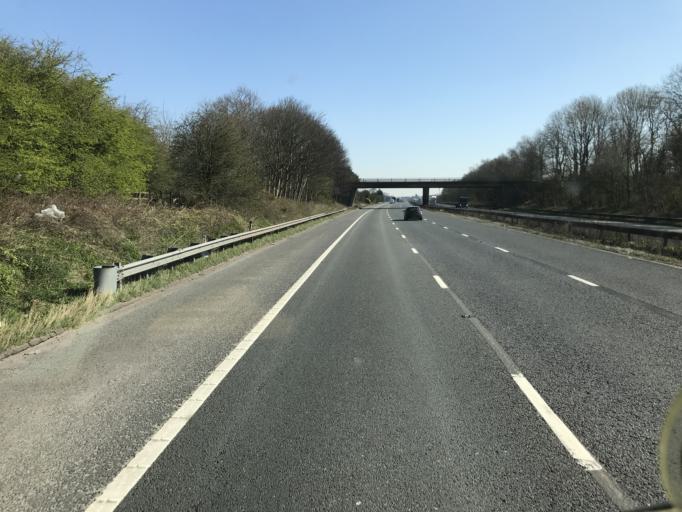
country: GB
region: England
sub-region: Warrington
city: Stretton
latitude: 53.3330
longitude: -2.6000
